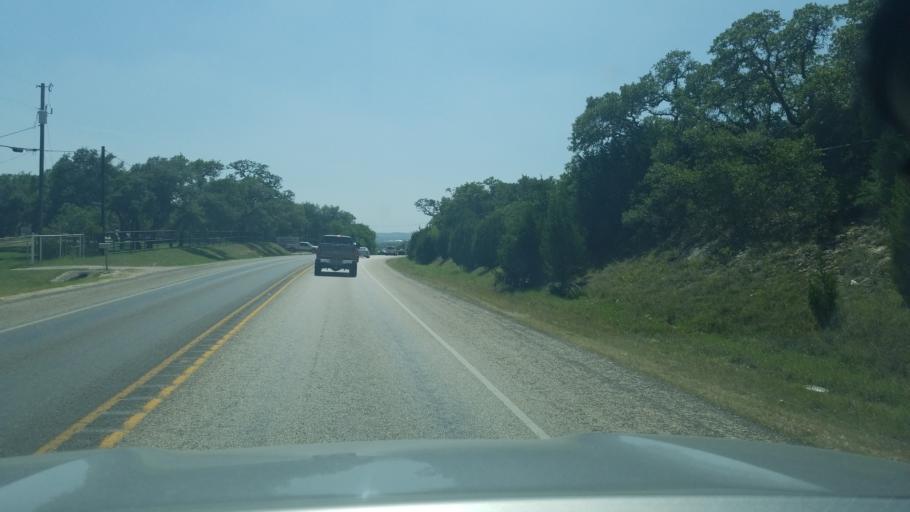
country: US
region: Texas
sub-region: Kendall County
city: Boerne
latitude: 29.7892
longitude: -98.6840
